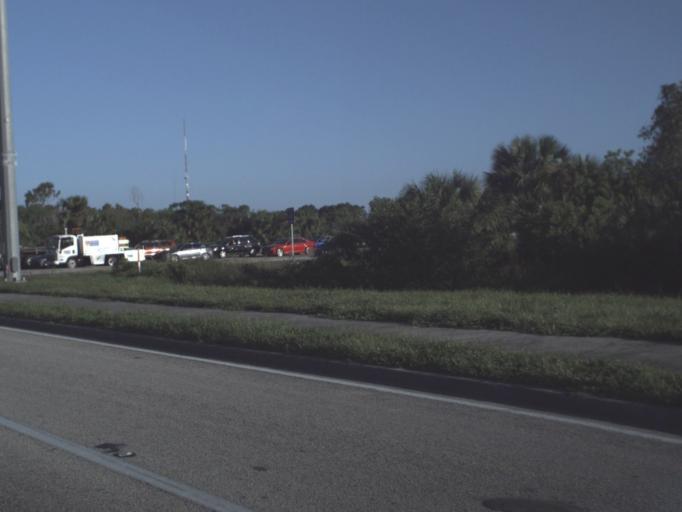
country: US
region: Florida
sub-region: Lee County
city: San Carlos Park
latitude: 26.4950
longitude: -81.8488
